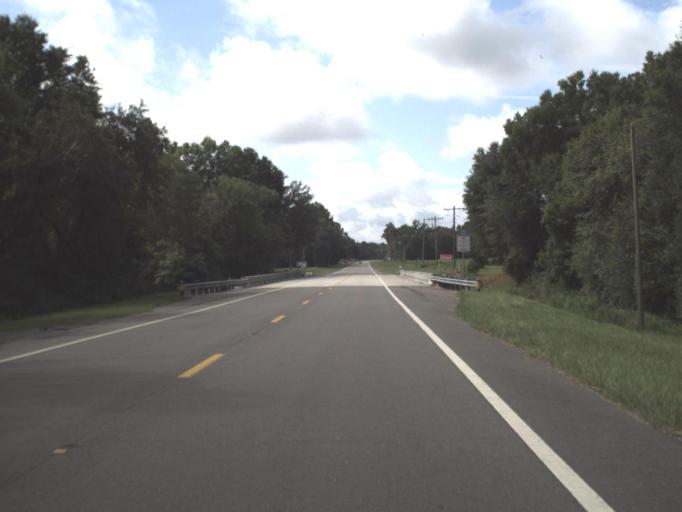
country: US
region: Florida
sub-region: Columbia County
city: Five Points
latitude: 30.3666
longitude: -82.6205
